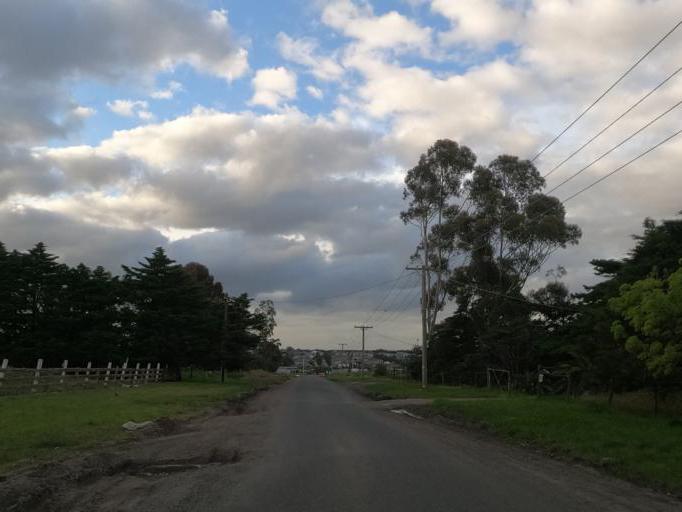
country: AU
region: Victoria
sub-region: Hume
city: Greenvale
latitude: -37.6321
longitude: 144.8857
